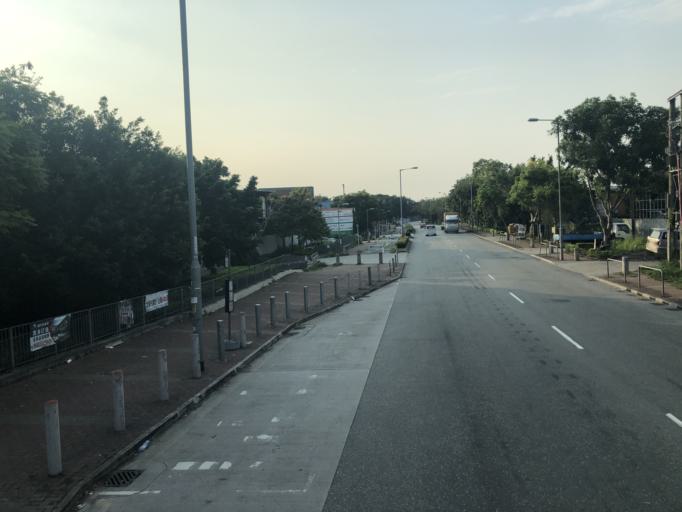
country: HK
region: Yuen Long
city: Yuen Long Kau Hui
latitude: 22.4565
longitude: 113.9918
